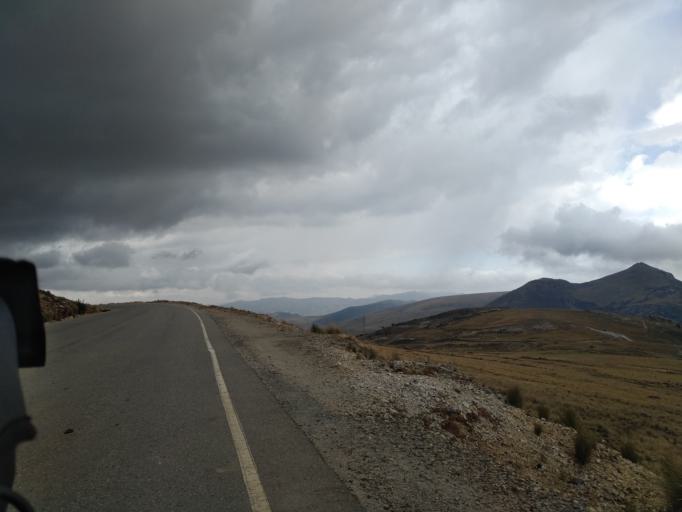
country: PE
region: La Libertad
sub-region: Provincia de Santiago de Chuco
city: Quiruvilca
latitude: -7.9926
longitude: -78.2996
